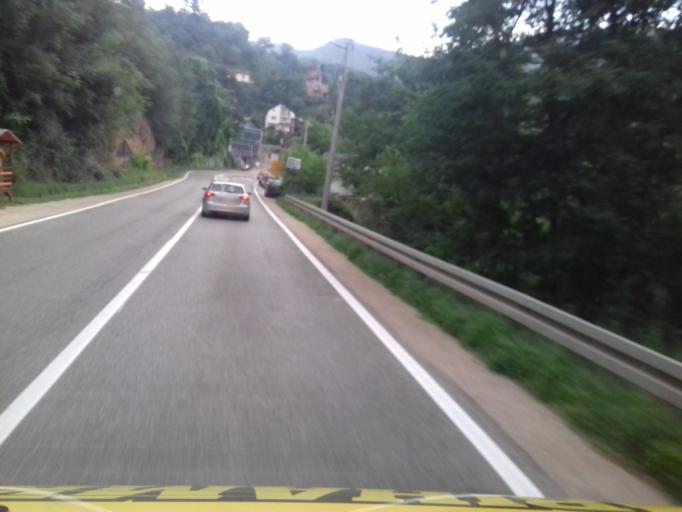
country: BA
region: Federation of Bosnia and Herzegovina
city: Jablanica
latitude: 43.6869
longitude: 17.8303
